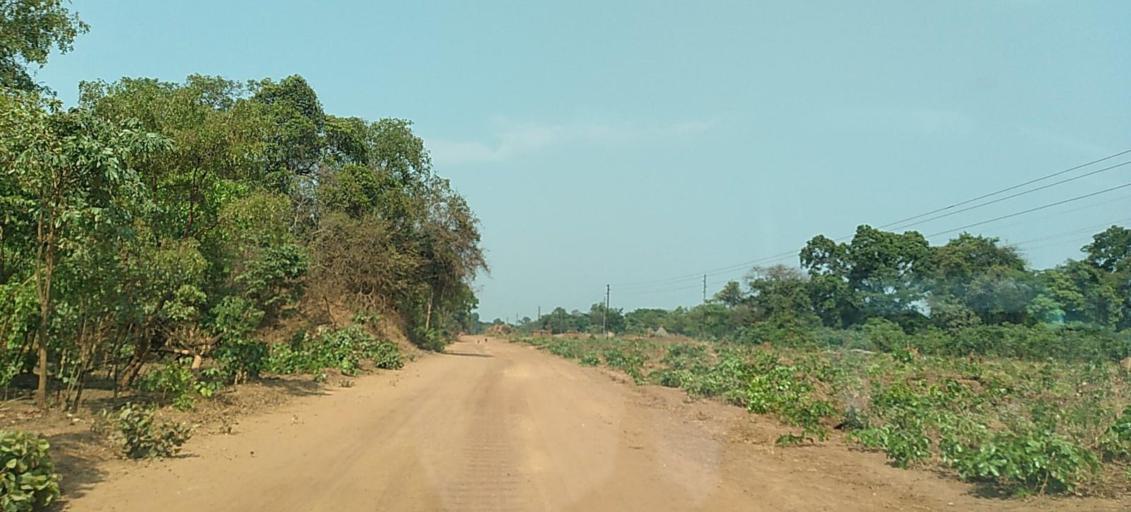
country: ZM
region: Copperbelt
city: Chingola
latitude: -13.0436
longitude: 27.4400
